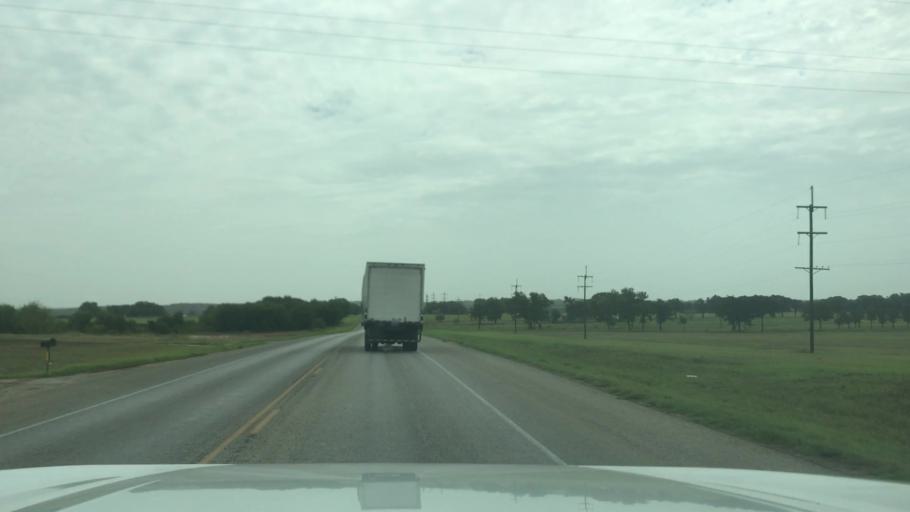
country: US
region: Texas
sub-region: Comanche County
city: De Leon
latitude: 32.0985
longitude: -98.4672
